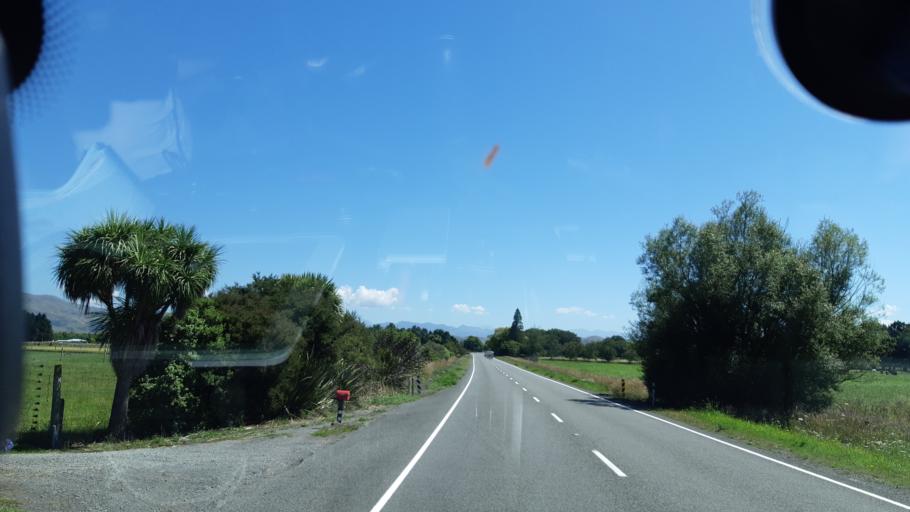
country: NZ
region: Canterbury
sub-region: Kaikoura District
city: Kaikoura
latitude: -42.7452
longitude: 173.2671
